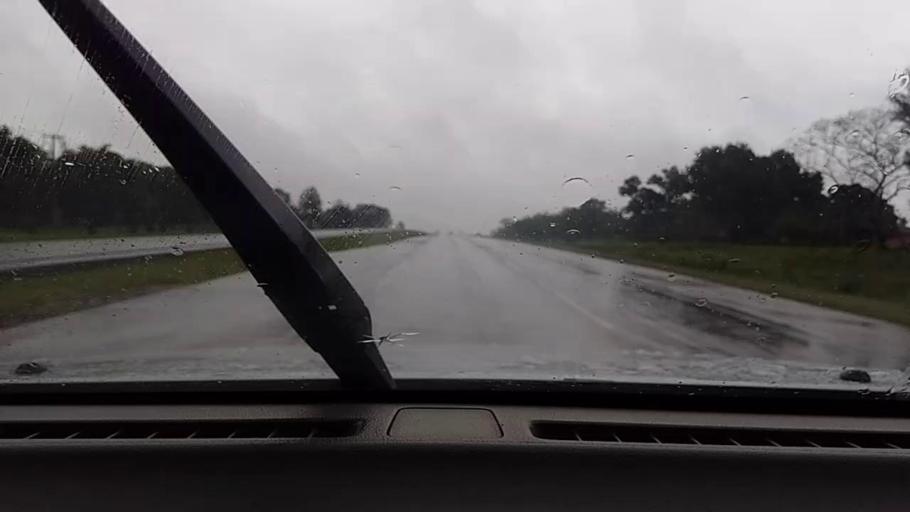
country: PY
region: Caaguazu
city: Repatriacion
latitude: -25.4661
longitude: -55.9425
